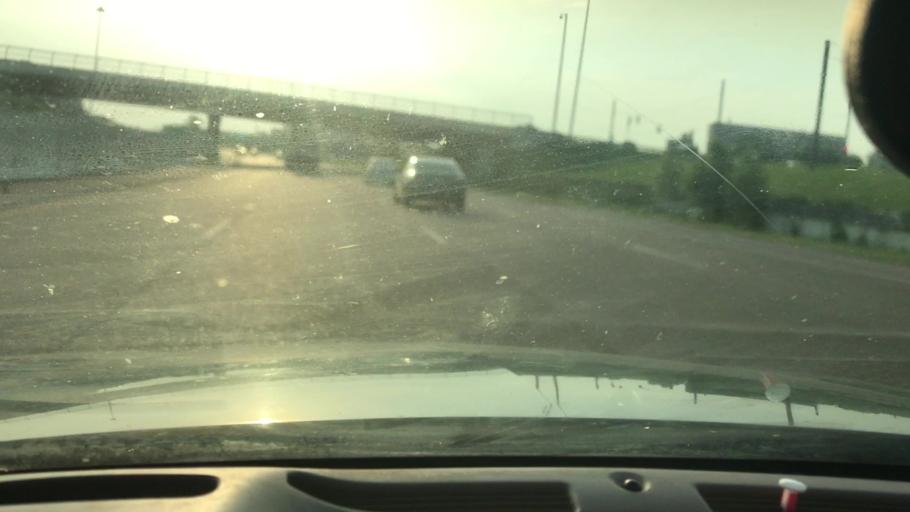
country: US
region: Tennessee
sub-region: Shelby County
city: Germantown
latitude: 35.0780
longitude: -89.9082
